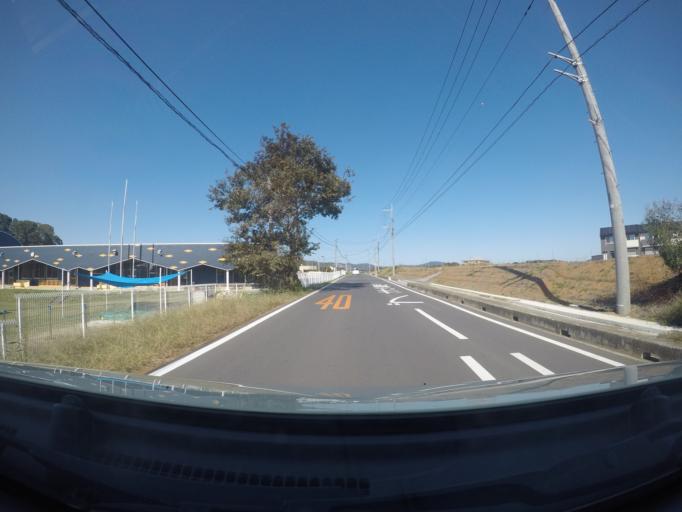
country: JP
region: Ibaraki
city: Naka
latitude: 36.1049
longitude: 140.1208
